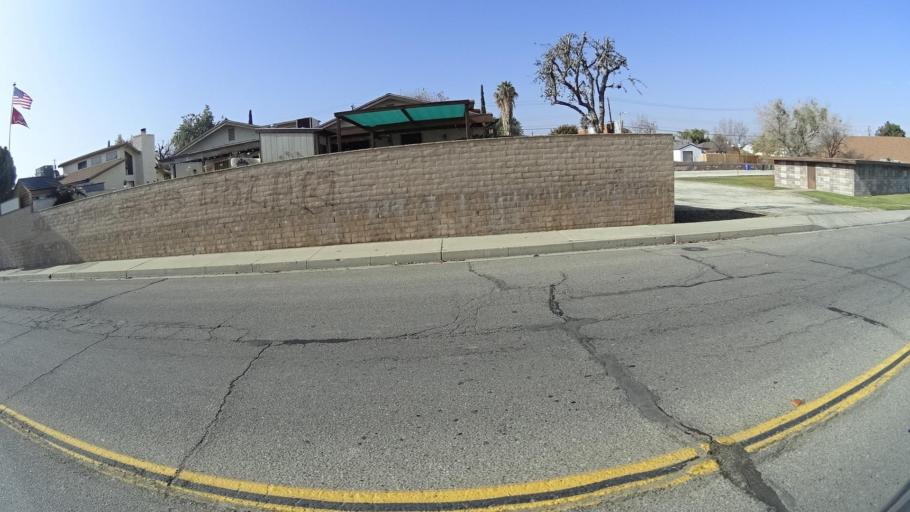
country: US
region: California
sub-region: Kern County
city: Taft Heights
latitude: 35.1385
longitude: -119.4651
